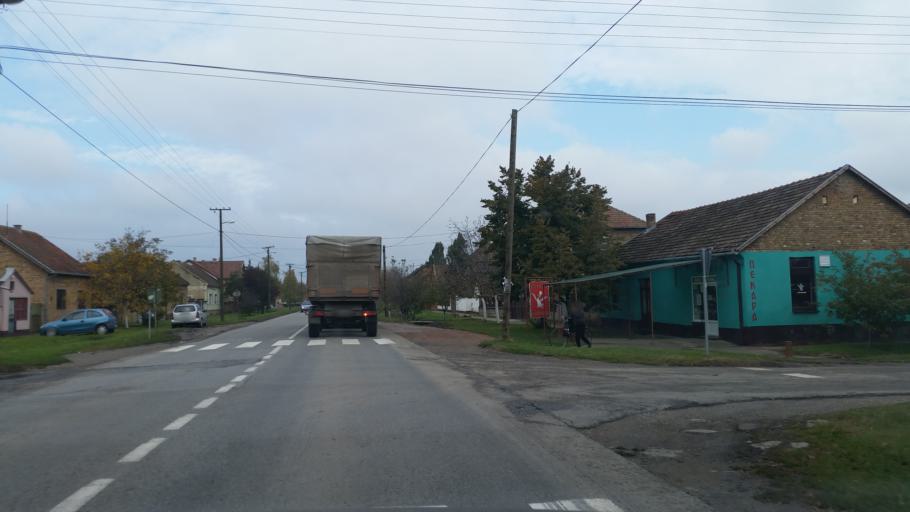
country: RS
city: Melenci
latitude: 45.5102
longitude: 20.3183
